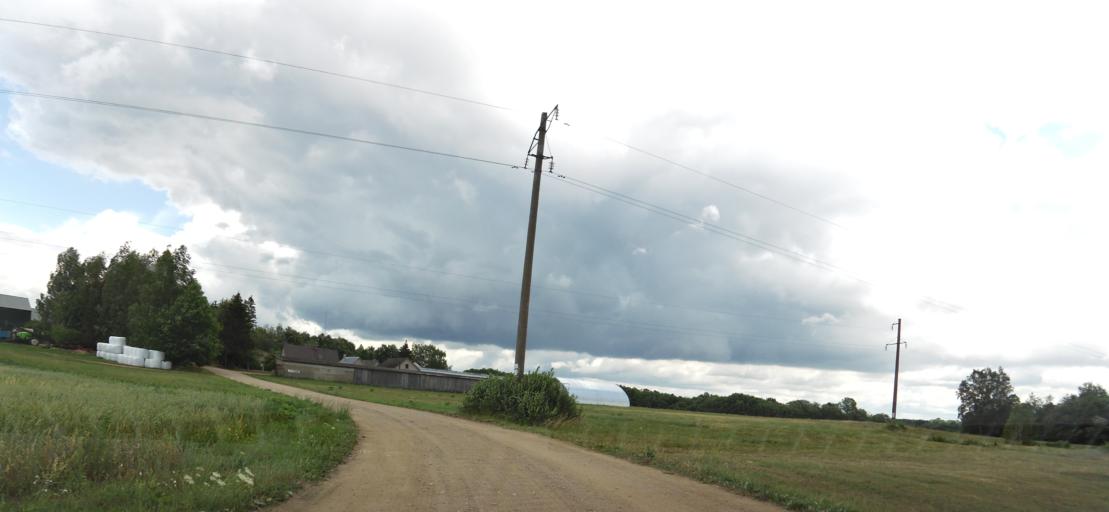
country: LT
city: Kupiskis
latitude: 55.8366
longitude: 24.9315
